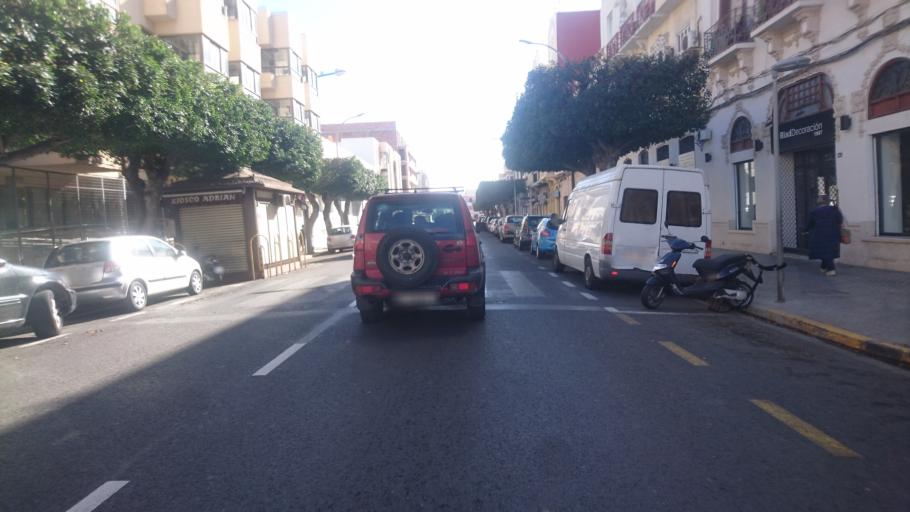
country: ES
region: Melilla
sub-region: Melilla
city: Melilla
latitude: 35.2834
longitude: -2.9419
